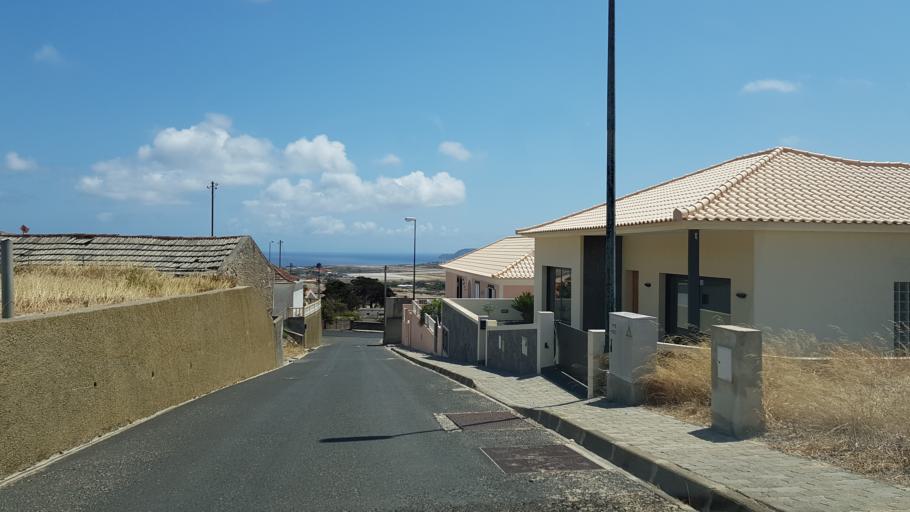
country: PT
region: Madeira
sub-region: Porto Santo
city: Camacha
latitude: 33.0875
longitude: -16.3415
